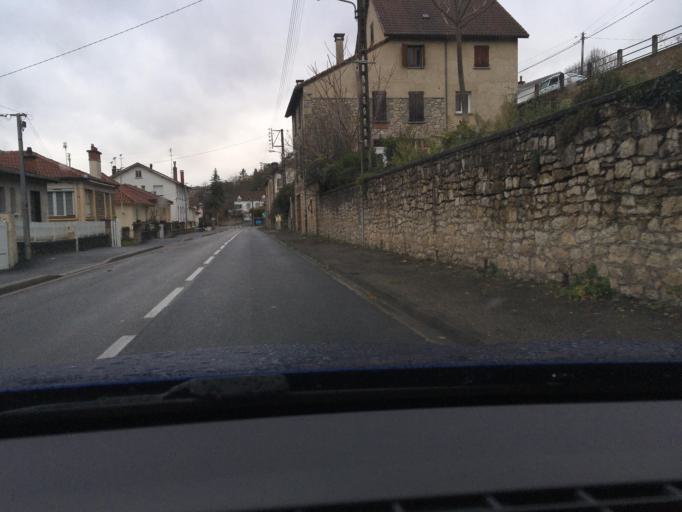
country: FR
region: Midi-Pyrenees
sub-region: Departement de l'Aveyron
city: Villefranche-de-Rouergue
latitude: 44.3574
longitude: 2.0286
